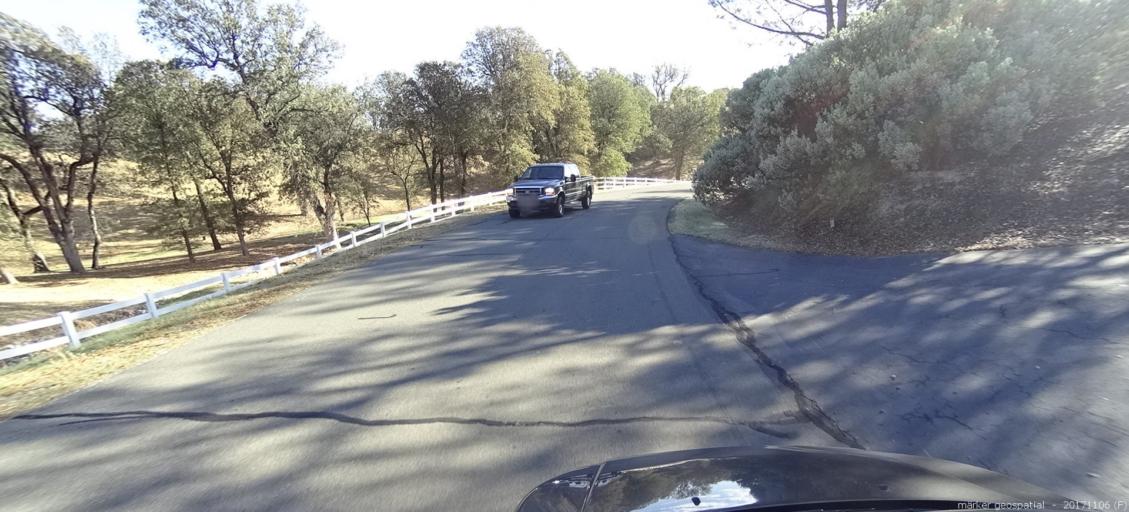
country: US
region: California
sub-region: Shasta County
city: Palo Cedro
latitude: 40.5031
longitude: -122.2403
